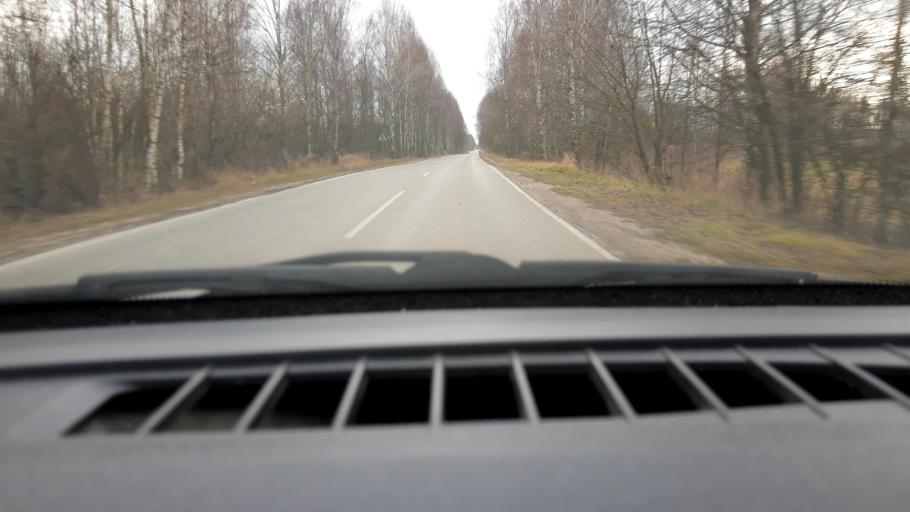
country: RU
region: Nizjnij Novgorod
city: Neklyudovo
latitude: 56.4678
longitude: 43.8927
